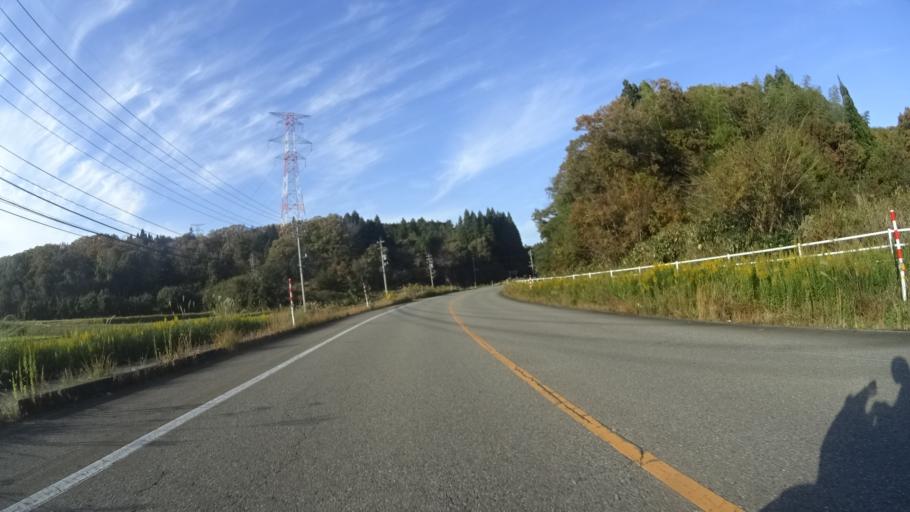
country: JP
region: Ishikawa
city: Hakui
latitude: 37.0473
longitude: 136.7744
